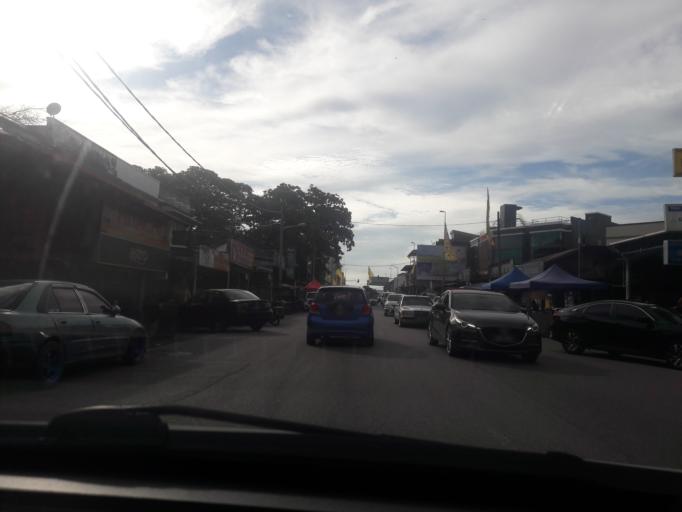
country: MY
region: Kedah
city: Sungai Petani
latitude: 5.6380
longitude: 100.4945
